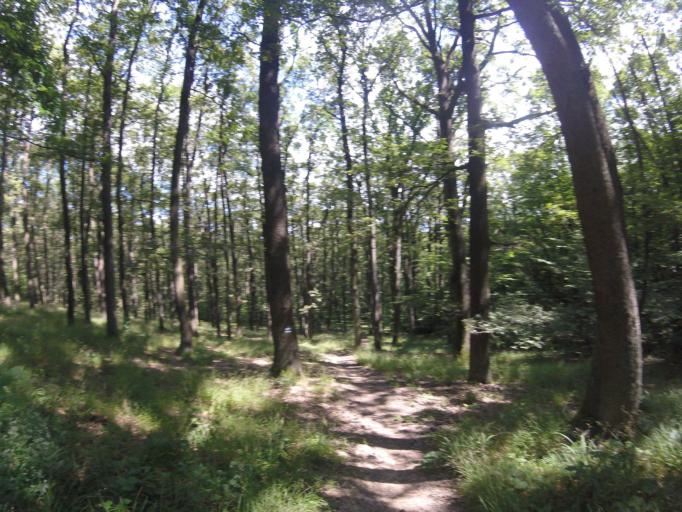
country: HU
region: Nograd
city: Romhany
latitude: 47.8980
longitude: 19.2409
